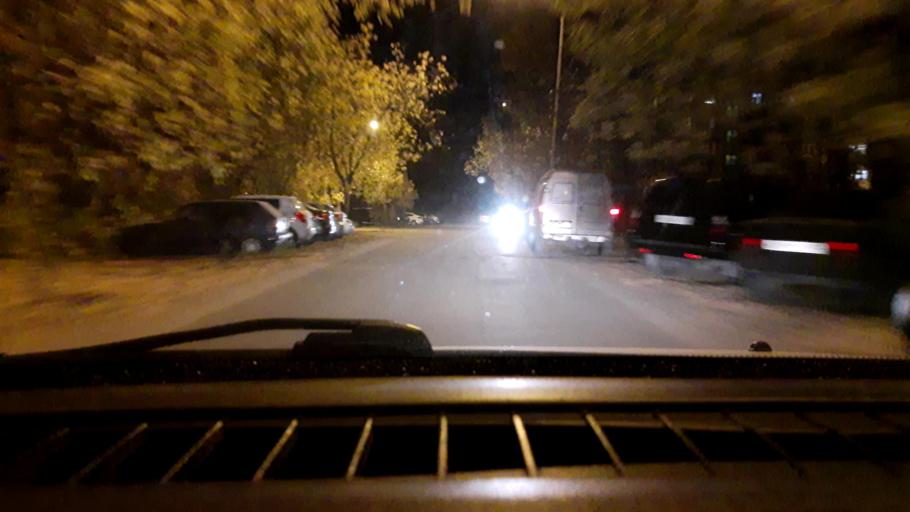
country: RU
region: Nizjnij Novgorod
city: Gorbatovka
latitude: 56.3579
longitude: 43.8364
